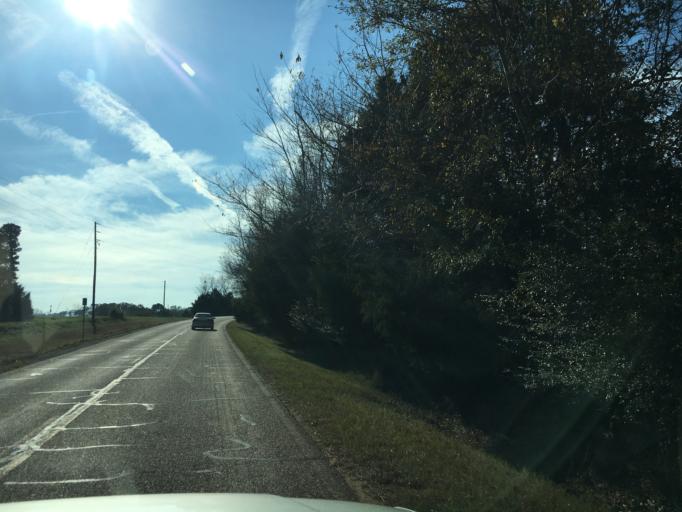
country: US
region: Georgia
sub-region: Hart County
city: Hartwell
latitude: 34.3113
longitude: -82.8164
